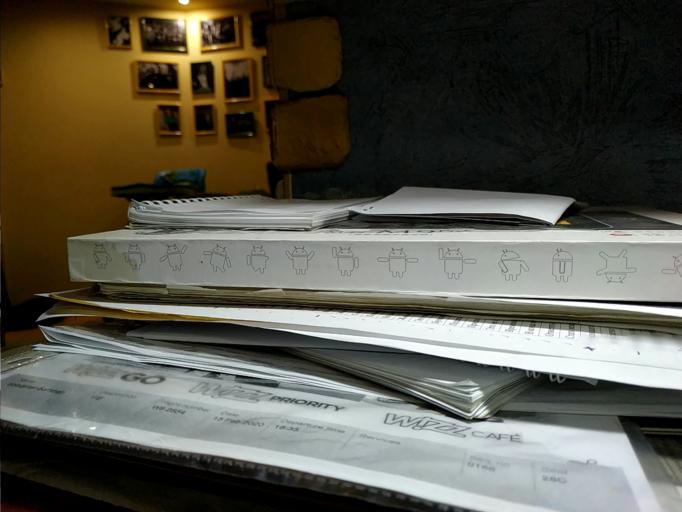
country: RU
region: Arkhangelskaya
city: Kargopol'
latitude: 61.6117
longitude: 39.2576
